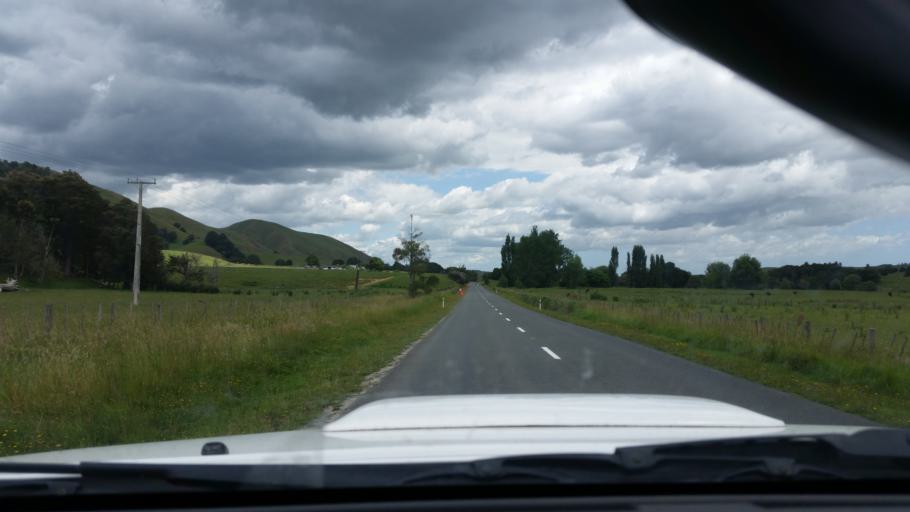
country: NZ
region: Northland
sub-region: Kaipara District
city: Dargaville
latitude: -35.8034
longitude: 173.9195
